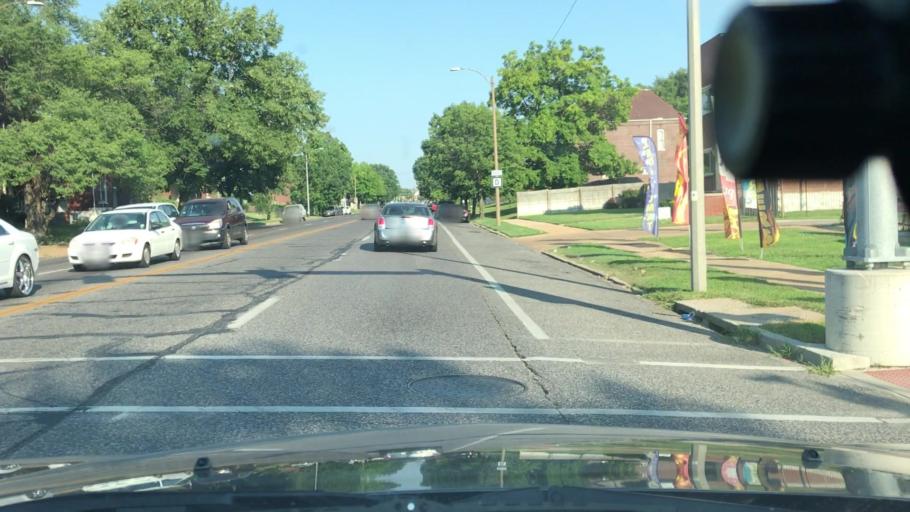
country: US
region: Missouri
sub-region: City of Saint Louis
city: St. Louis
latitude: 38.6487
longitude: -90.2338
